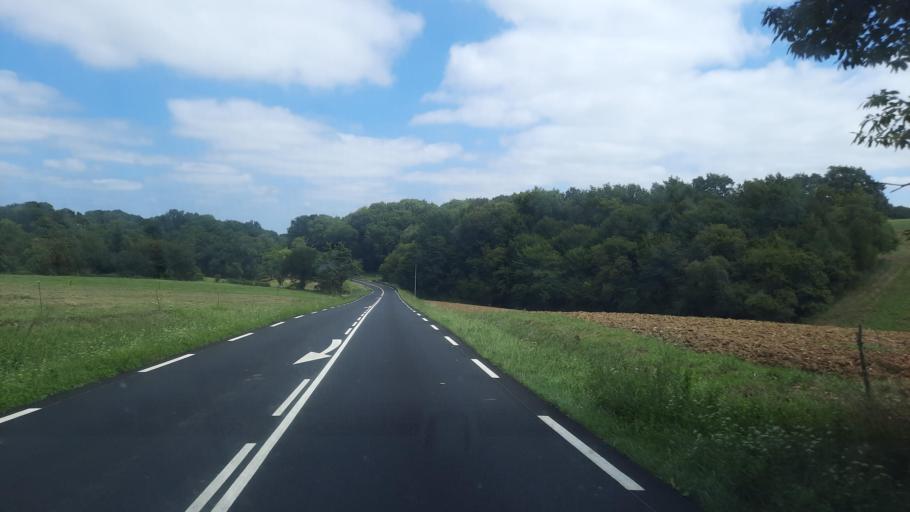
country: FR
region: Midi-Pyrenees
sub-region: Departement de la Haute-Garonne
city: Boulogne-sur-Gesse
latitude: 43.2920
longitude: 0.5721
